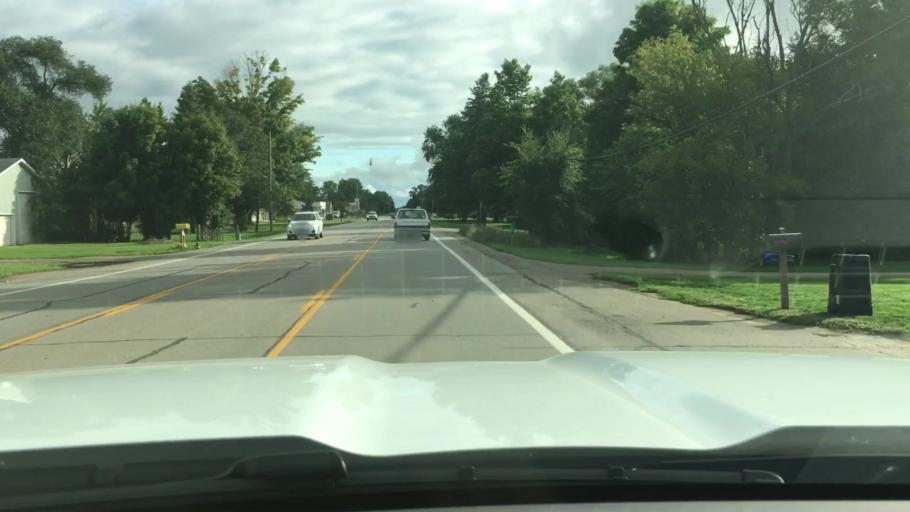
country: US
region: Michigan
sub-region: Tuscola County
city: Caro
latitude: 43.5002
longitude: -83.3816
